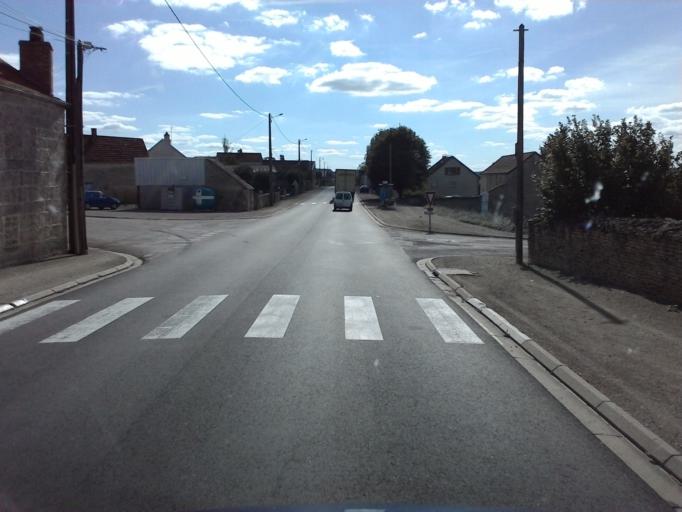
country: FR
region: Bourgogne
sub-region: Departement de la Cote-d'Or
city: Chatillon-sur-Seine
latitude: 47.8126
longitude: 4.5313
